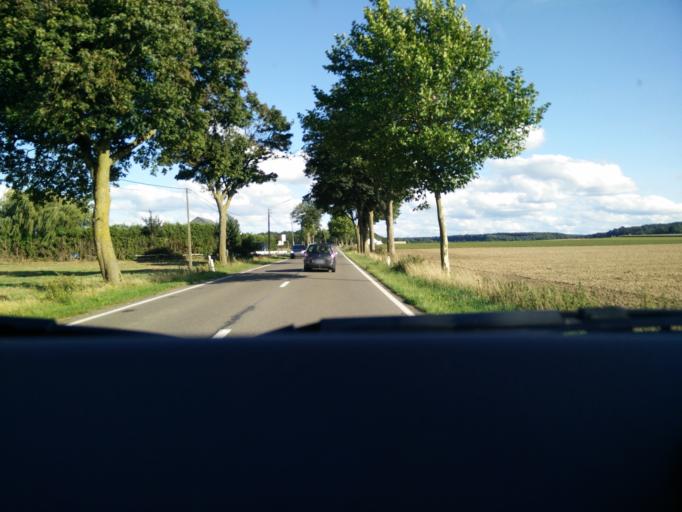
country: BE
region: Wallonia
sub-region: Province du Hainaut
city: Merbes-le-Chateau
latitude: 50.2931
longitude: 4.1687
